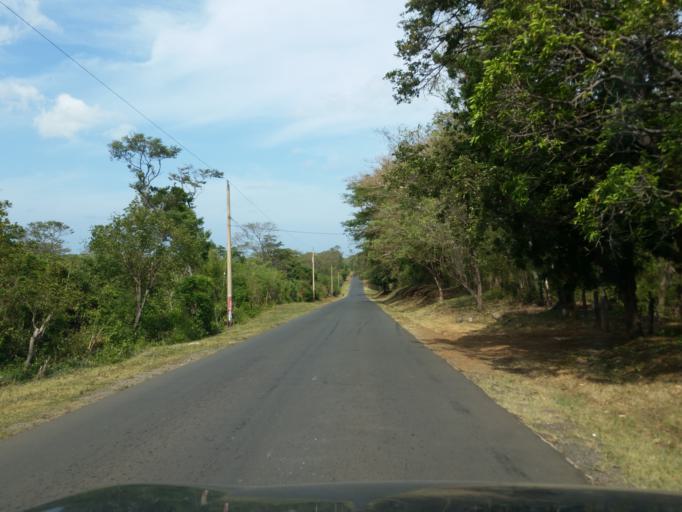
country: NI
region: Managua
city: San Rafael del Sur
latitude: 11.9111
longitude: -86.3769
